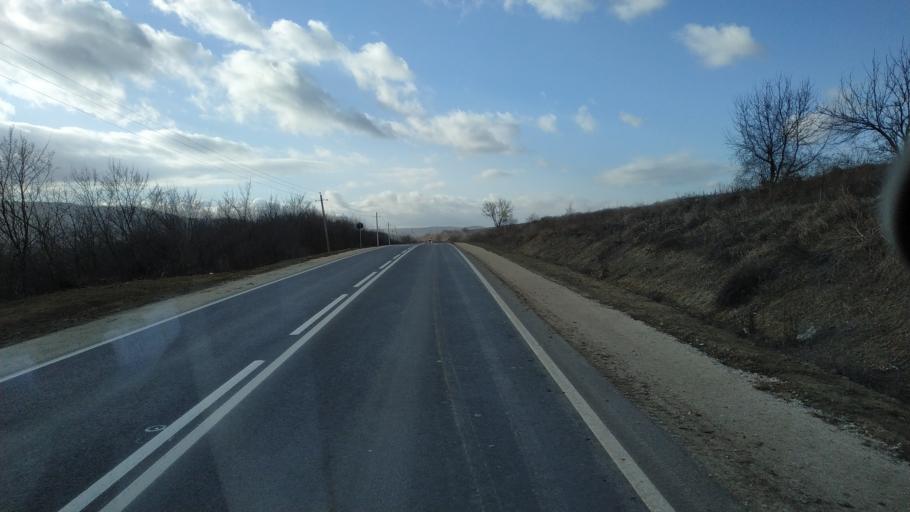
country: MD
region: Calarasi
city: Calarasi
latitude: 47.2918
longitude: 28.1779
